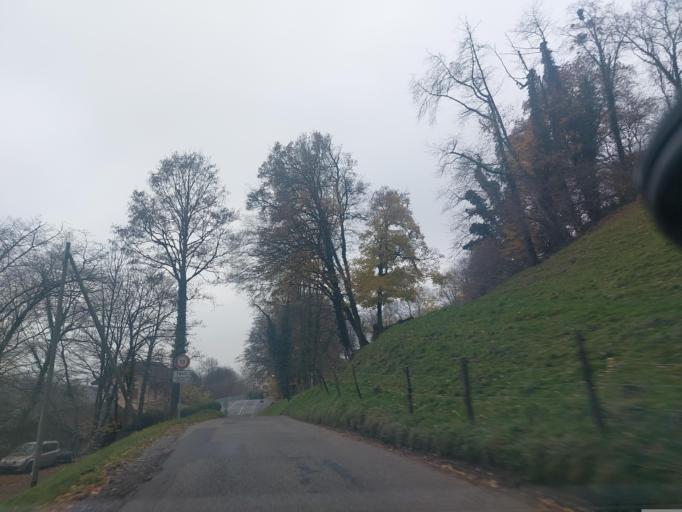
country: CH
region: Vaud
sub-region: Riviera-Pays-d'Enhaut District
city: Jongny
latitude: 46.4873
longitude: 6.8709
